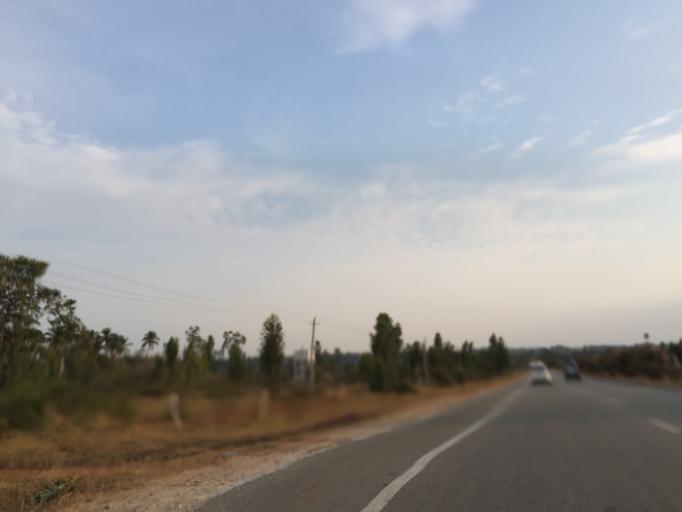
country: IN
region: Karnataka
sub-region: Chikkaballapur
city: Chik Ballapur
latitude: 13.3997
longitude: 77.7422
